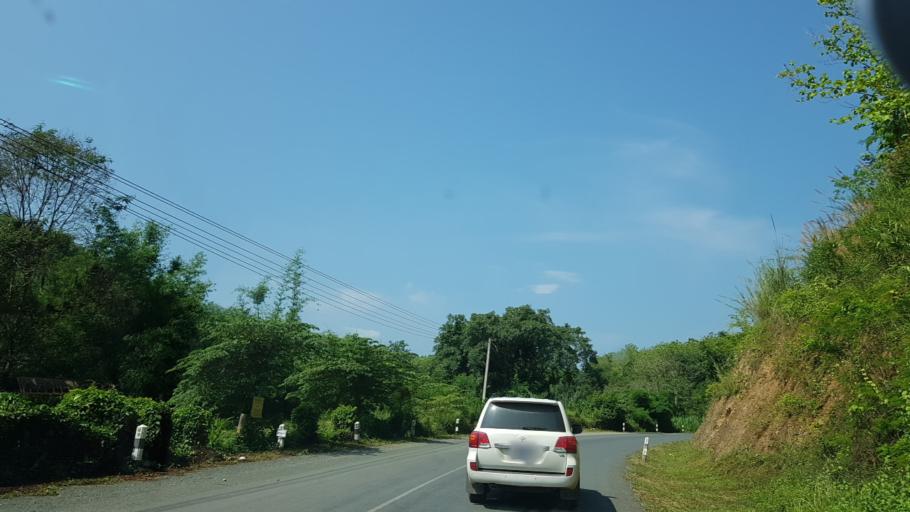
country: LA
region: Louangphabang
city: Xiang Ngeun
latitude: 19.7249
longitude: 102.1518
